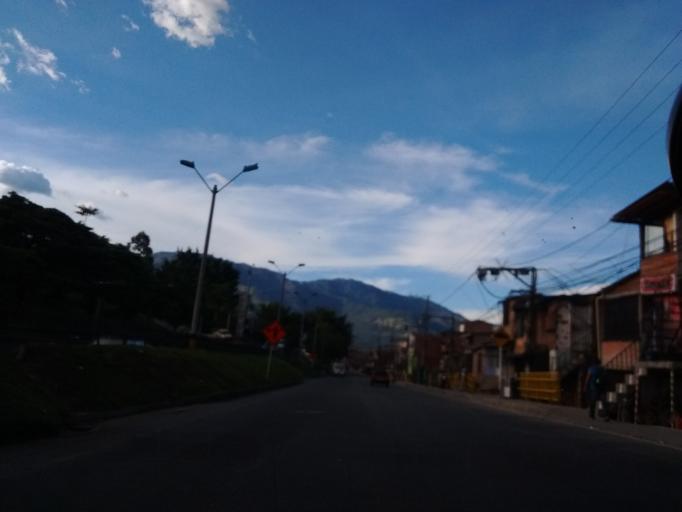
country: CO
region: Antioquia
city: Bello
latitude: 6.3010
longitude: -75.5587
